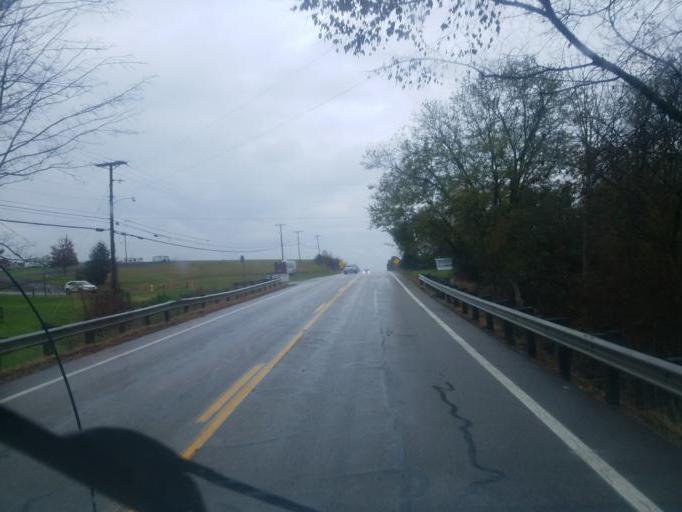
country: US
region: Ohio
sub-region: Muskingum County
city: Frazeysburg
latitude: 40.0382
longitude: -82.1165
